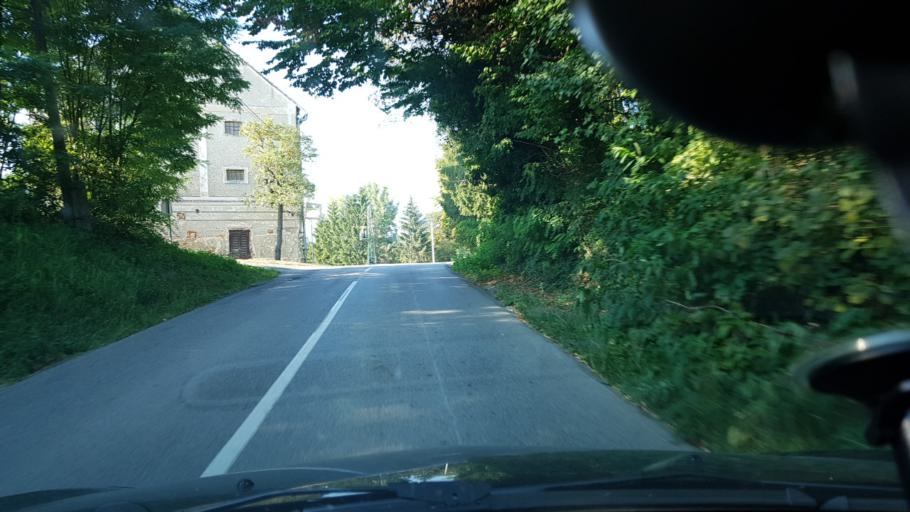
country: SI
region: Bistrica ob Sotli
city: Bistrica ob Sotli
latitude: 46.0243
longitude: 15.7297
